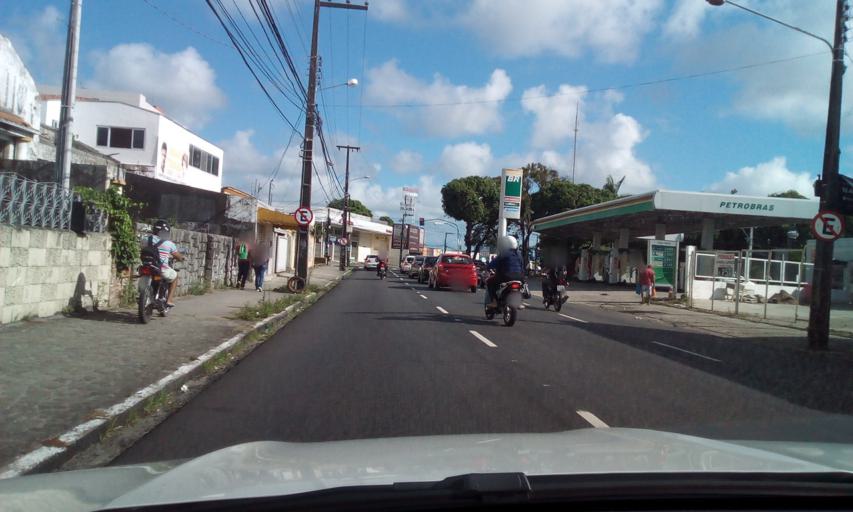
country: BR
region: Paraiba
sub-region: Joao Pessoa
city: Joao Pessoa
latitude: -7.1270
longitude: -34.8791
